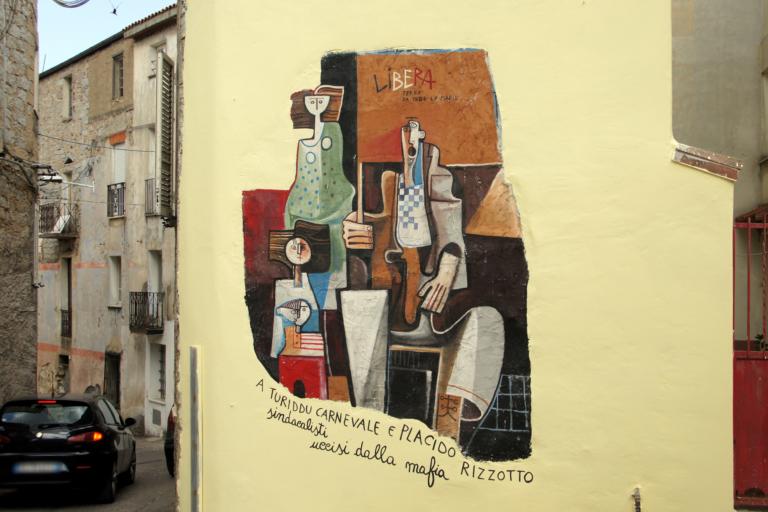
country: IT
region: Sardinia
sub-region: Provincia di Nuoro
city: Orgosolo
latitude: 40.2022
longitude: 9.3539
